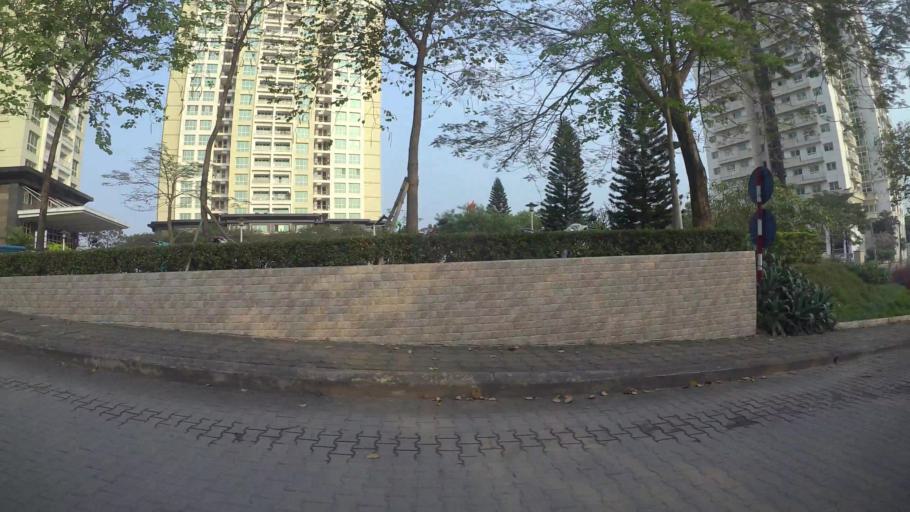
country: VN
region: Ha Noi
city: Tay Ho
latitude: 21.0787
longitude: 105.7924
